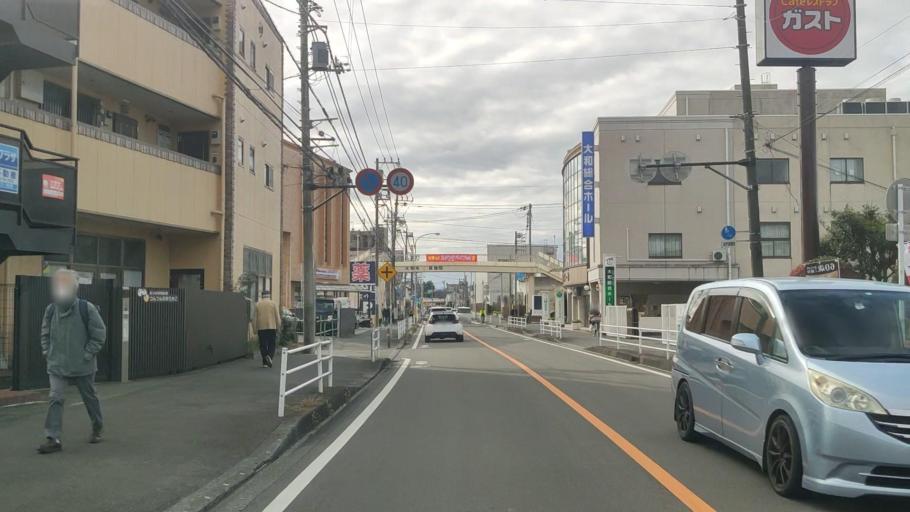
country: JP
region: Kanagawa
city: Minami-rinkan
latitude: 35.4859
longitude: 139.4451
